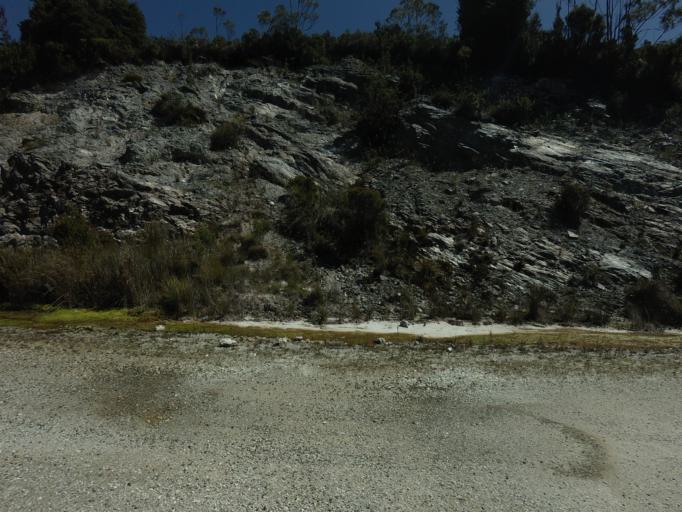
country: AU
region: Tasmania
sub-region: West Coast
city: Queenstown
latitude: -42.7700
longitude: 145.9846
